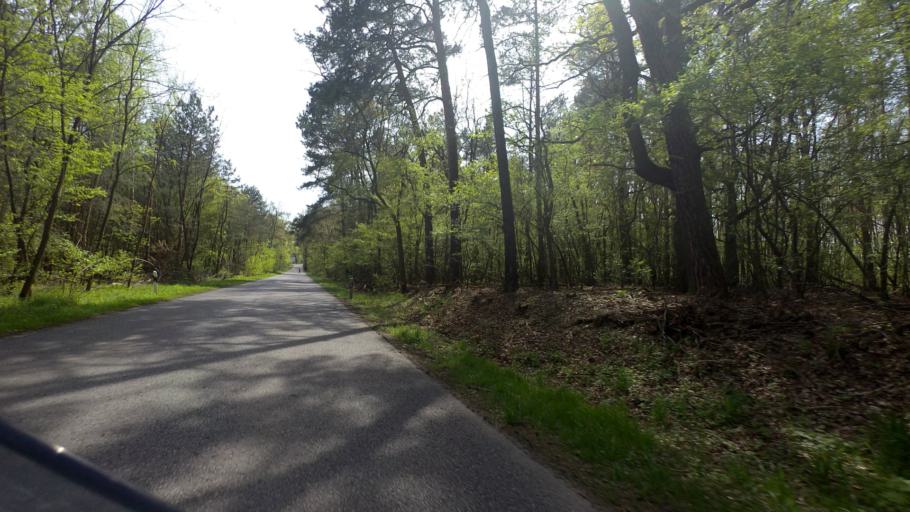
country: DE
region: Berlin
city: Kladow
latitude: 52.4899
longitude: 13.1237
